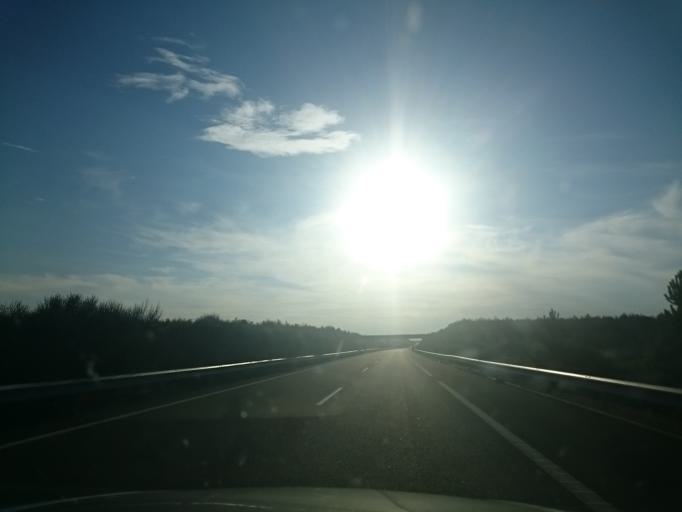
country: ES
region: Castille and Leon
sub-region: Provincia de Palencia
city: Ledigos
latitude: 42.3605
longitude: -4.8391
